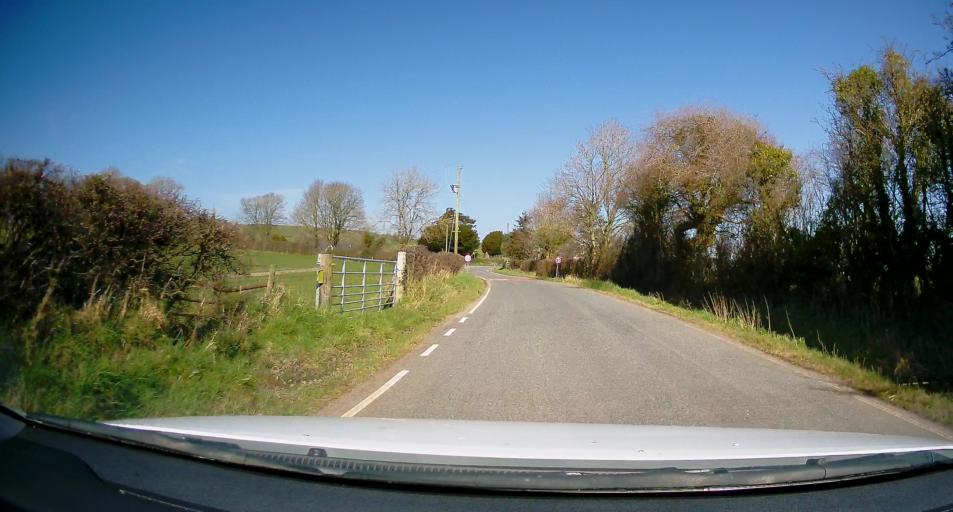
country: GB
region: Wales
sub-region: County of Ceredigion
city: Lledrod
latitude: 52.3132
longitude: -4.0606
